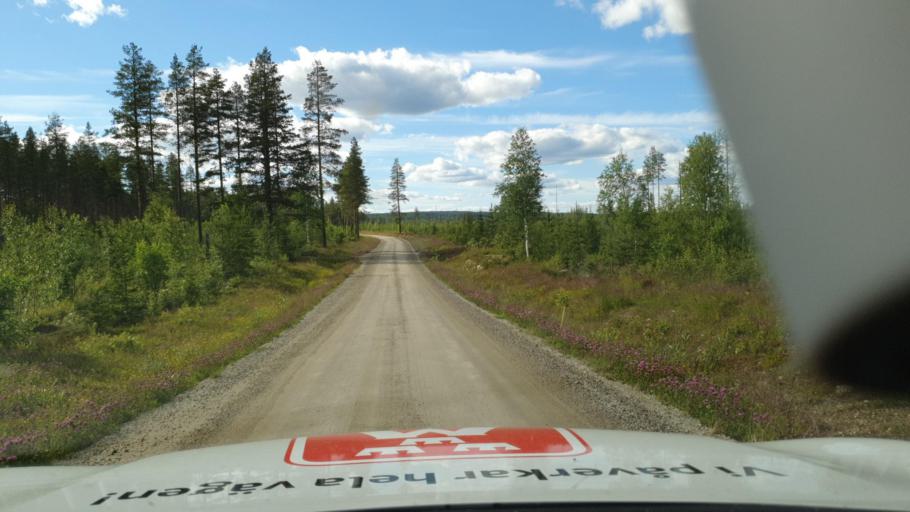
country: SE
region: Vaesterbotten
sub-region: Lycksele Kommun
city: Lycksele
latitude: 64.3955
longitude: 18.5849
